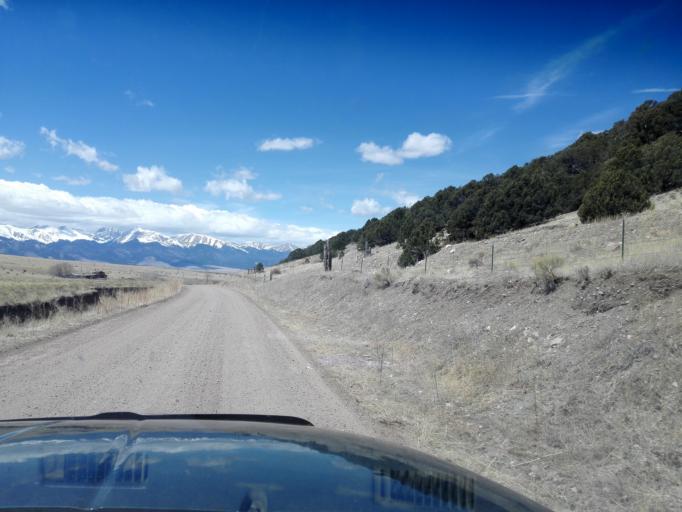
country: US
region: Colorado
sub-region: Custer County
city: Westcliffe
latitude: 37.9748
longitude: -105.2846
